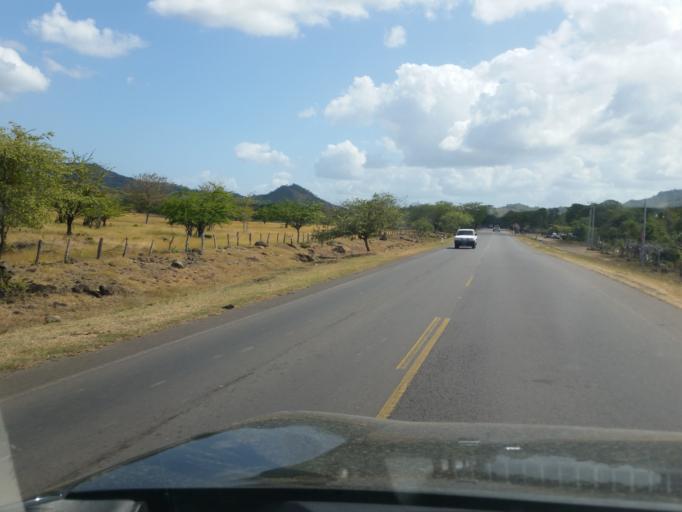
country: NI
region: Chontales
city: Comalapa
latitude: 12.1954
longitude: -85.6208
